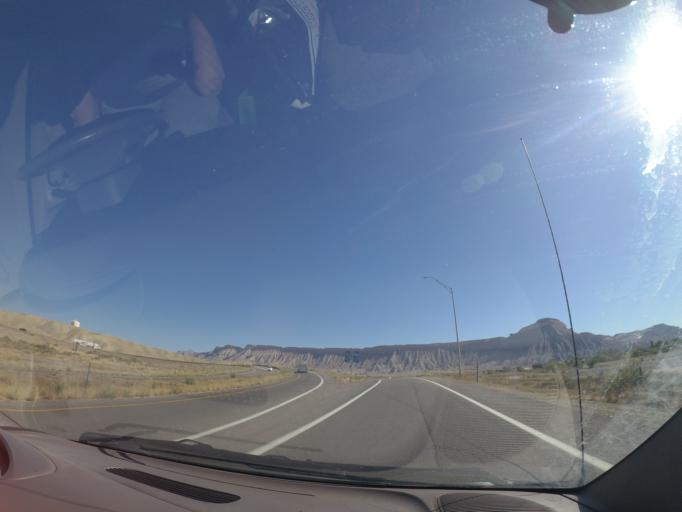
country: US
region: Colorado
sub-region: Mesa County
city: Clifton
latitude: 39.1010
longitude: -108.4476
